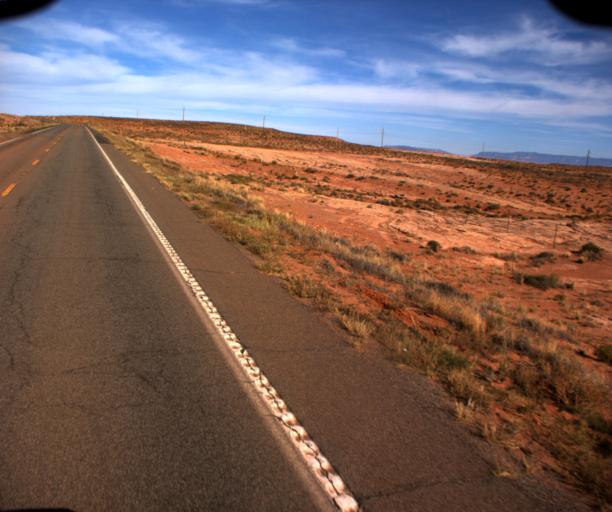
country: US
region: Arizona
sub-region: Navajo County
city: Kayenta
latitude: 36.8937
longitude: -109.7992
